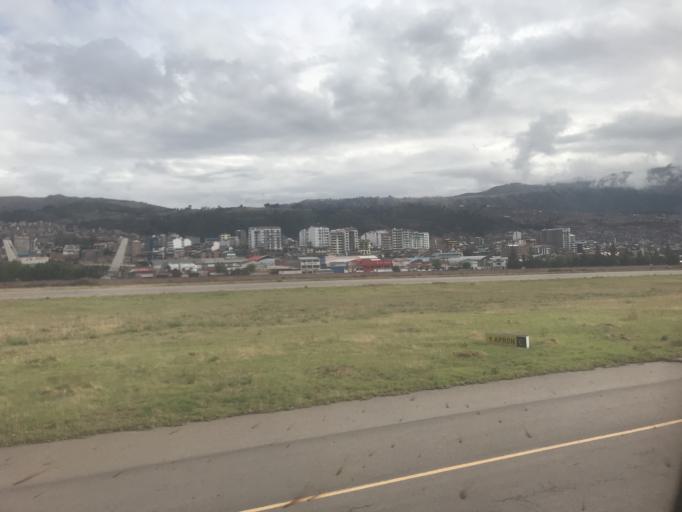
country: PE
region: Cusco
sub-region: Provincia de Cusco
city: Cusco
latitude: -13.5358
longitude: -71.9521
